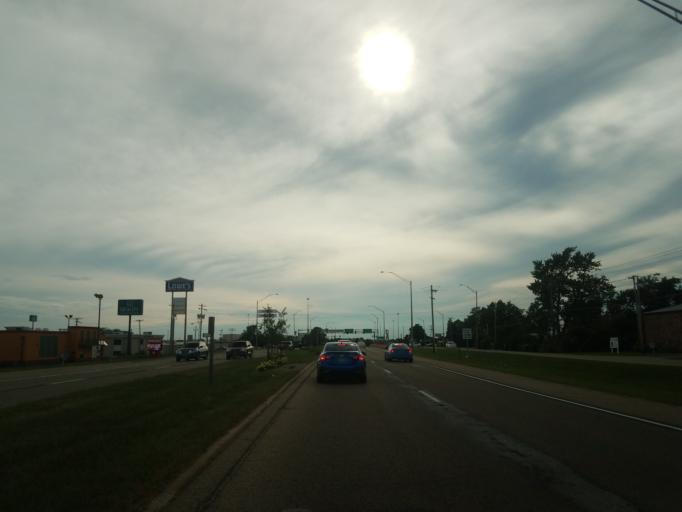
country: US
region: Illinois
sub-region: McLean County
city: Bloomington
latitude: 40.4883
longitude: -88.9470
